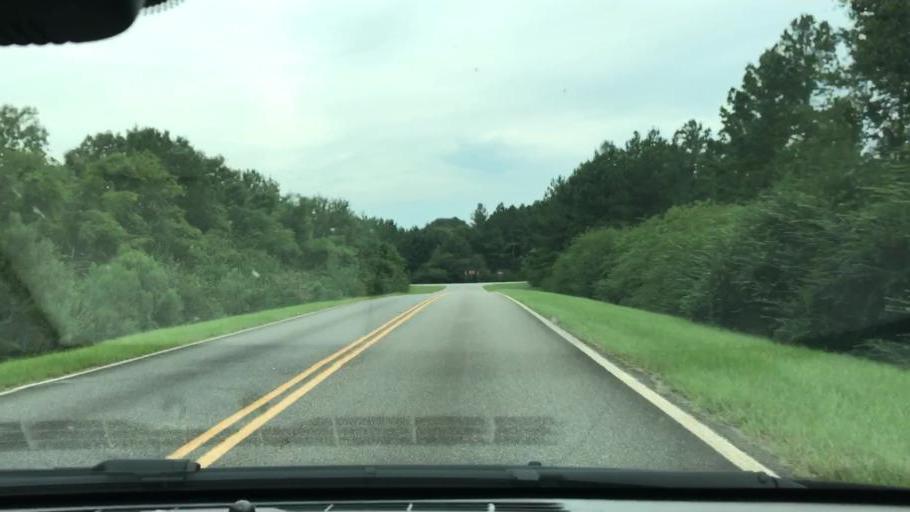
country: US
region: Georgia
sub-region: Early County
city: Blakely
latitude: 31.4116
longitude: -84.9249
